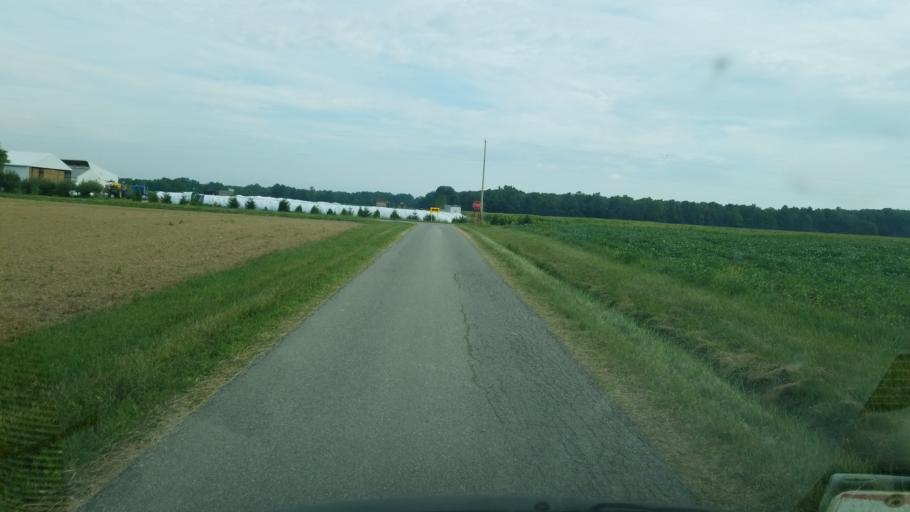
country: US
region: Ohio
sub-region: Crawford County
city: Bucyrus
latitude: 40.9496
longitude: -83.0356
